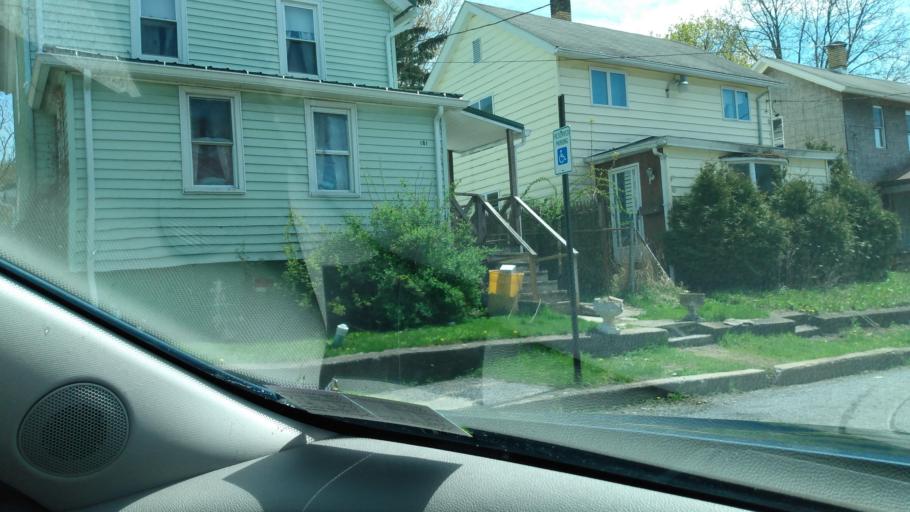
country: US
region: Pennsylvania
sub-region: Blair County
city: Bellwood
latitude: 40.6819
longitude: -78.4209
